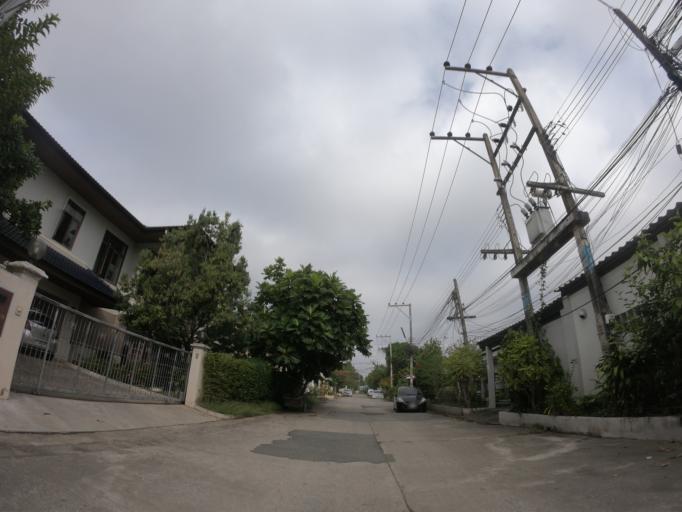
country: TH
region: Chiang Mai
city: Chiang Mai
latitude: 18.7592
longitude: 98.9771
